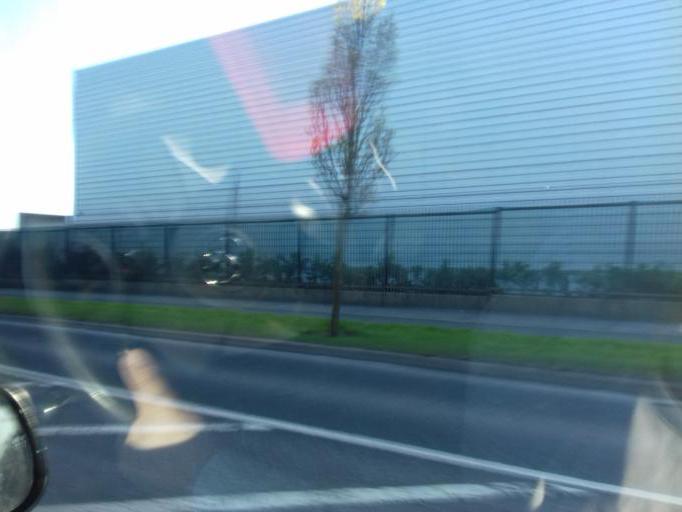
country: IE
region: Leinster
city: Castleknock
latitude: 53.4031
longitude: -6.3383
